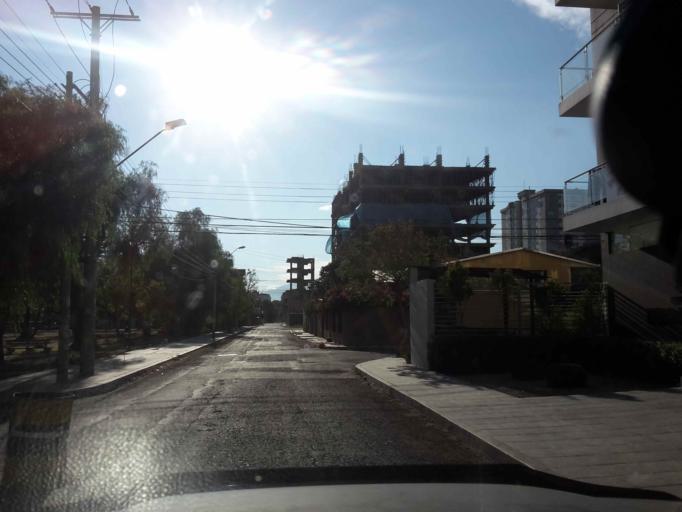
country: BO
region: Cochabamba
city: Cochabamba
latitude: -17.3732
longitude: -66.1775
